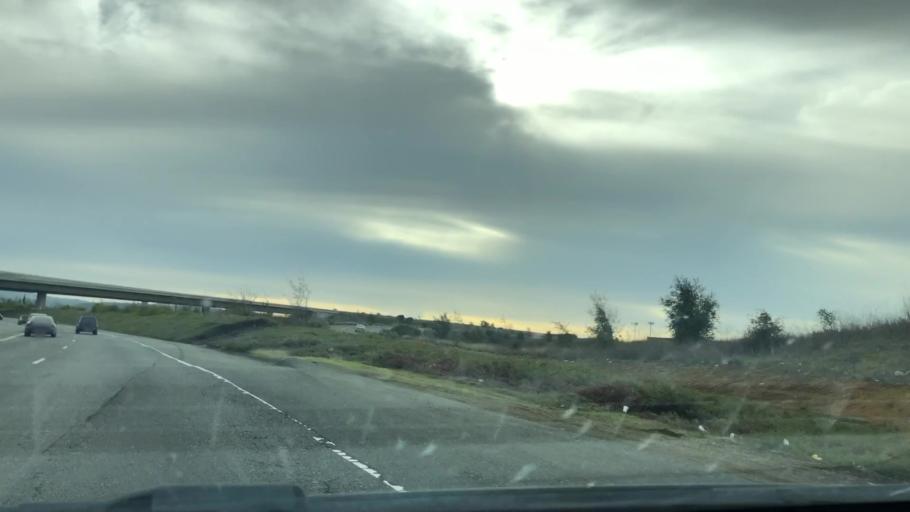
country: US
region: California
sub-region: Solano County
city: Benicia
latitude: 38.0535
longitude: -122.1304
